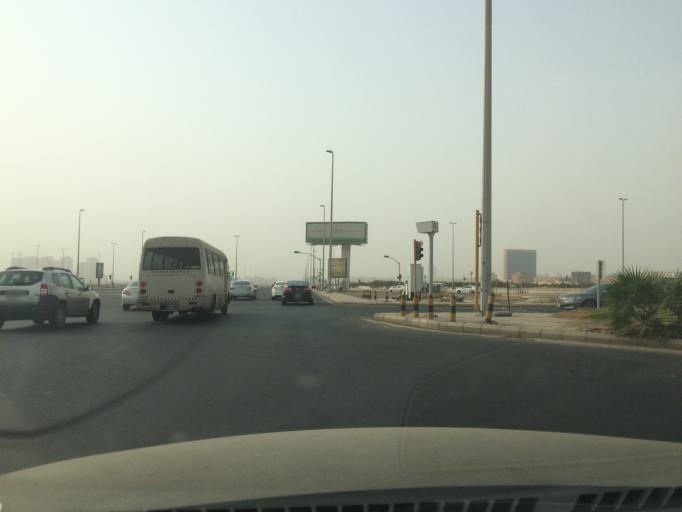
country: SA
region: Makkah
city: Jeddah
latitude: 21.4978
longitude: 39.2175
